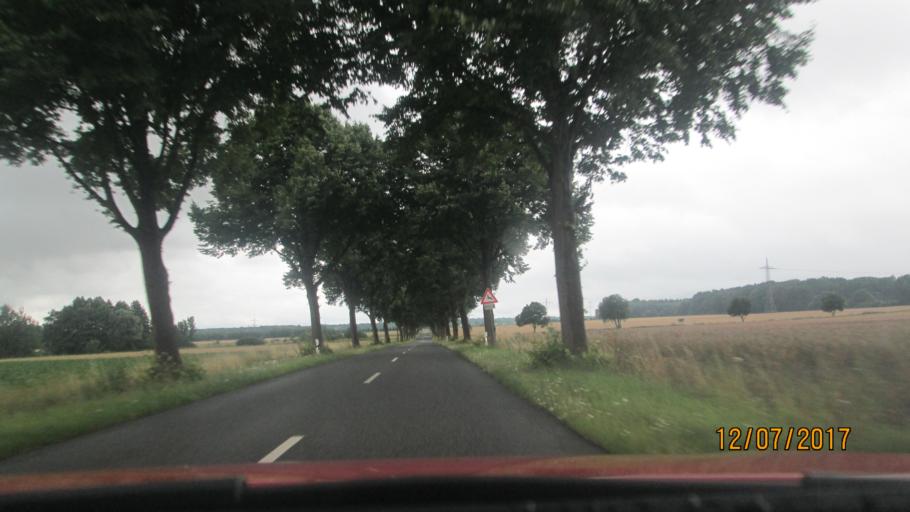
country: DE
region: Lower Saxony
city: Lehre
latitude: 52.3924
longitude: 10.6891
